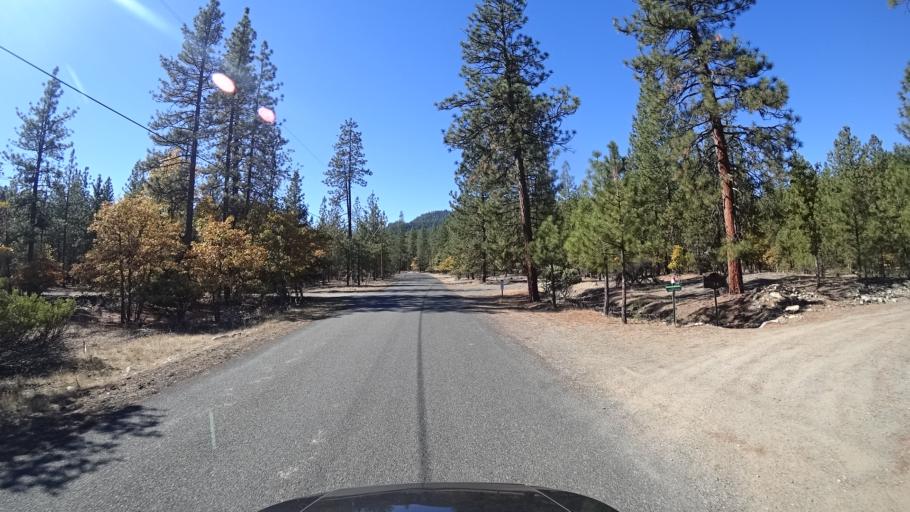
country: US
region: California
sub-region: Siskiyou County
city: Yreka
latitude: 41.5373
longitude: -122.9529
